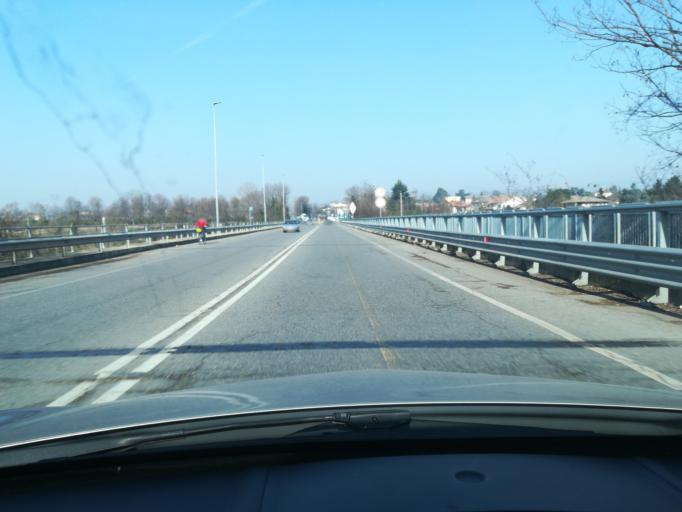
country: IT
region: Lombardy
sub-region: Provincia di Brescia
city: Palazzolo sull'Oglio
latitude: 45.5924
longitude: 9.8749
